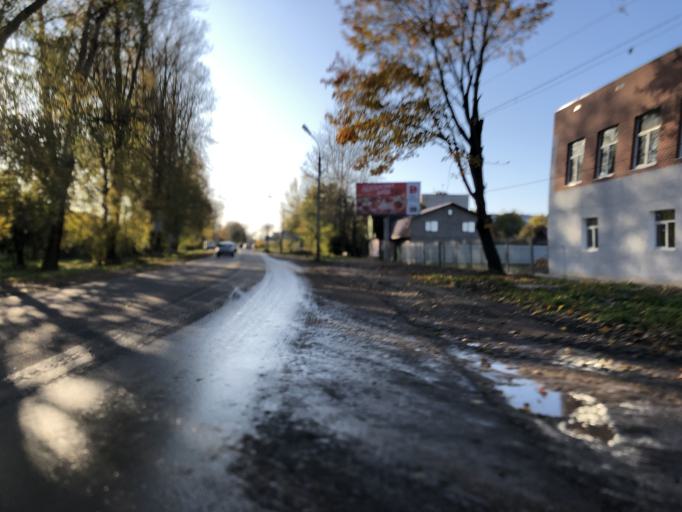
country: RU
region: Tverskaya
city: Rzhev
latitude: 56.2465
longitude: 34.3389
